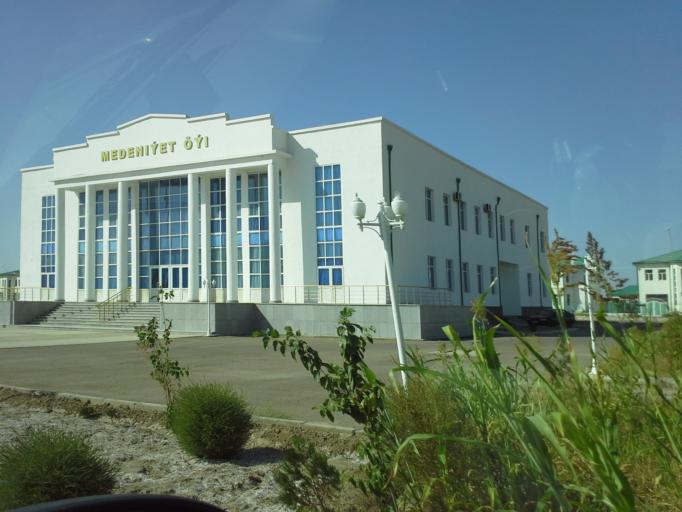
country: TM
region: Dasoguz
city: Dasoguz
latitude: 41.8145
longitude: 59.9585
